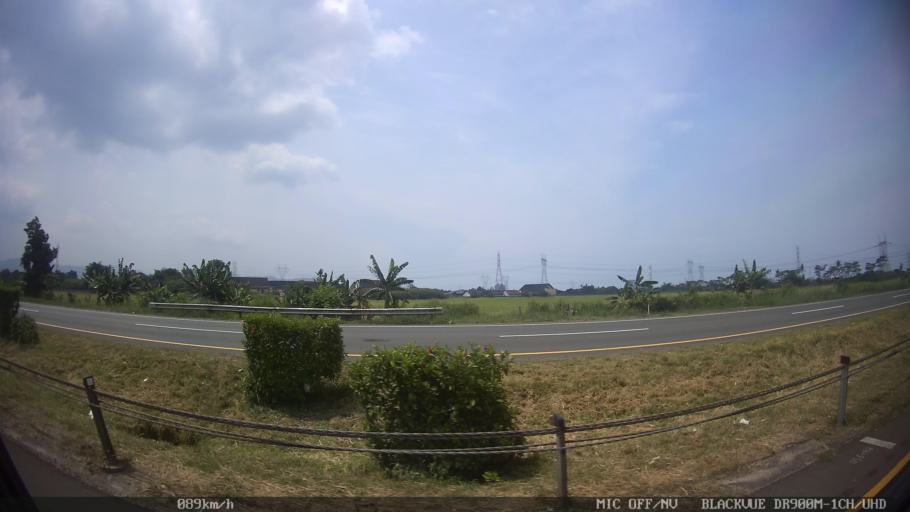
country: ID
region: Banten
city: Bojonegara
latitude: -6.0120
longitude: 106.0781
